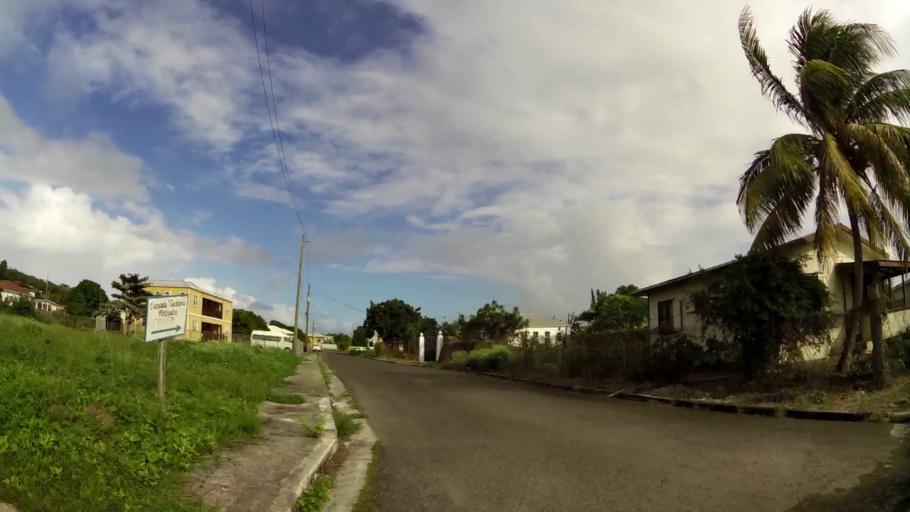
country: AG
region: Saint George
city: Piggotts
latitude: 17.1321
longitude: -61.8223
